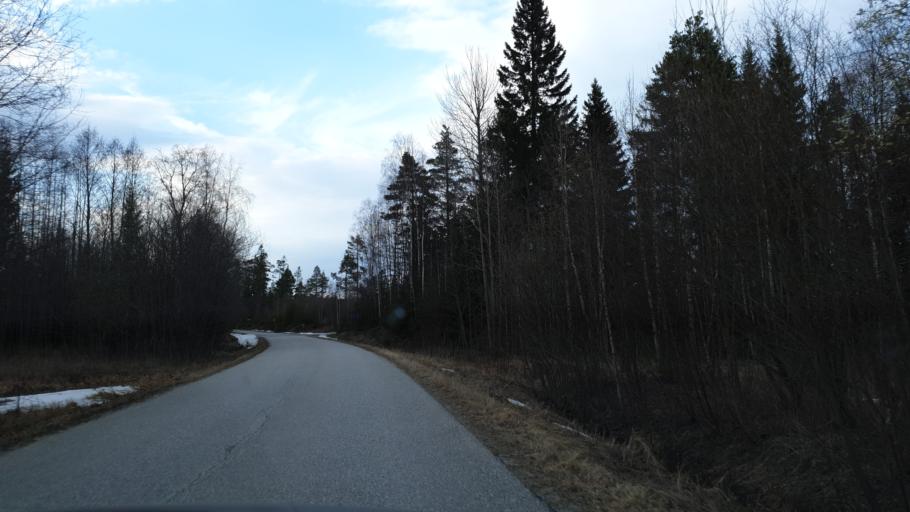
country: SE
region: Vaesternorrland
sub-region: Sundsvalls Kommun
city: Njurundabommen
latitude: 62.0223
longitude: 17.4073
